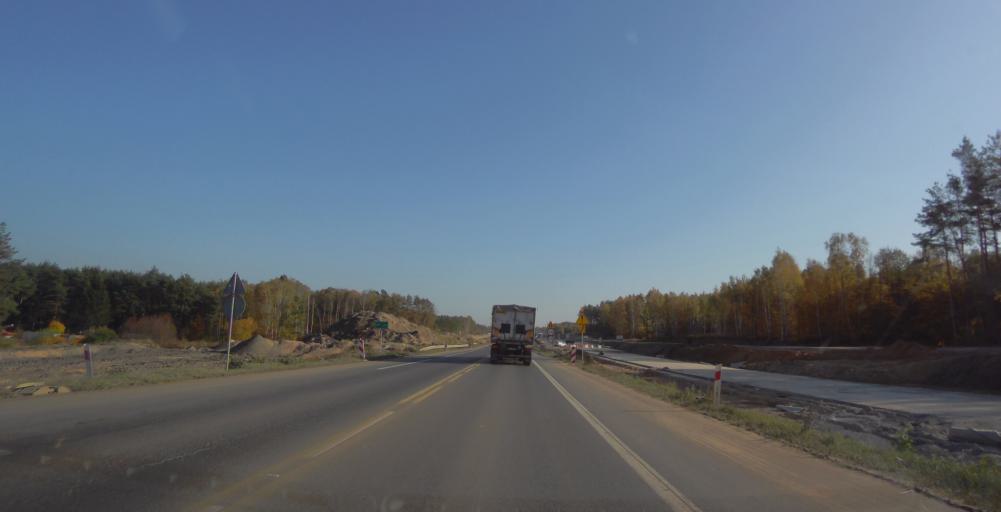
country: PL
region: Masovian Voivodeship
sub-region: Powiat otwocki
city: Celestynow
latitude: 52.1273
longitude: 21.3507
